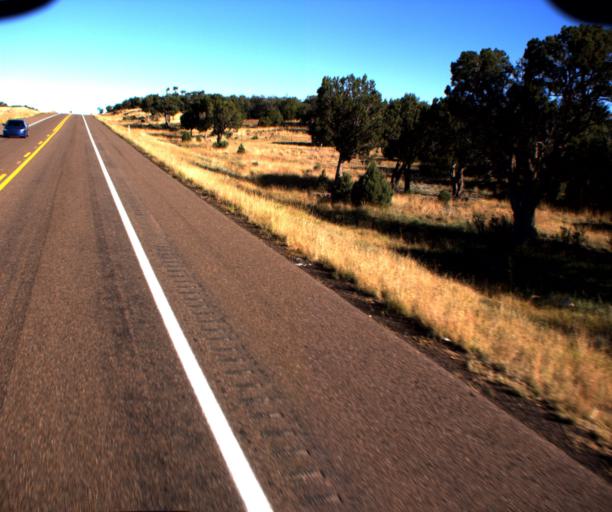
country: US
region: Arizona
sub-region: Navajo County
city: White Mountain Lake
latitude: 34.3284
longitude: -110.0460
